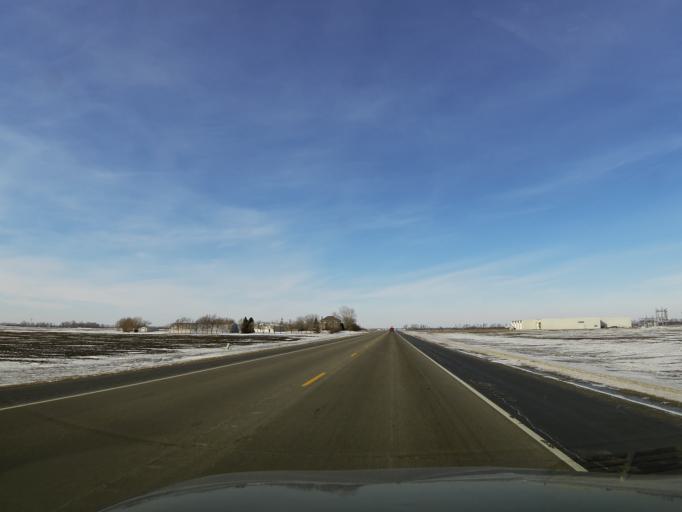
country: US
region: North Dakota
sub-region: Walsh County
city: Grafton
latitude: 48.4124
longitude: -97.3379
